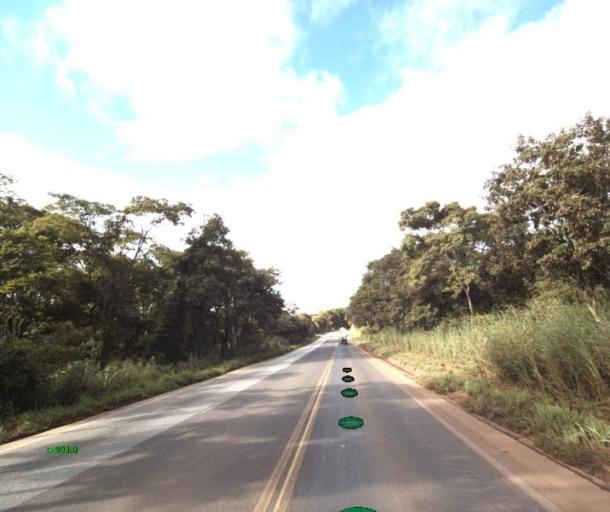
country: BR
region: Goias
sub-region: Uruacu
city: Uruacu
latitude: -14.5683
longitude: -49.1563
